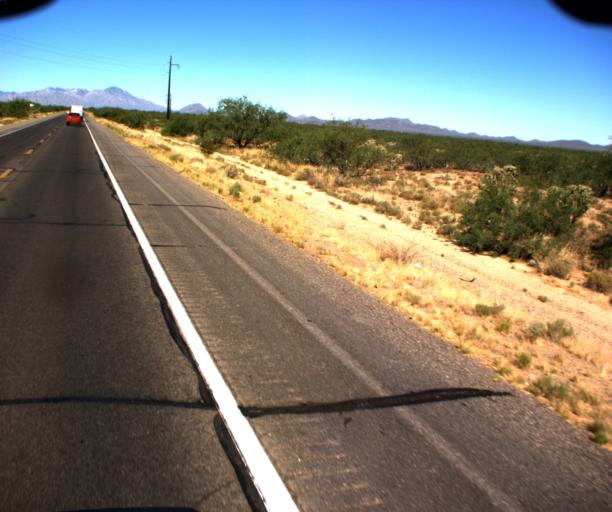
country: US
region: Arizona
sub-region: Pima County
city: Three Points
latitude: 32.1044
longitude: -111.2440
